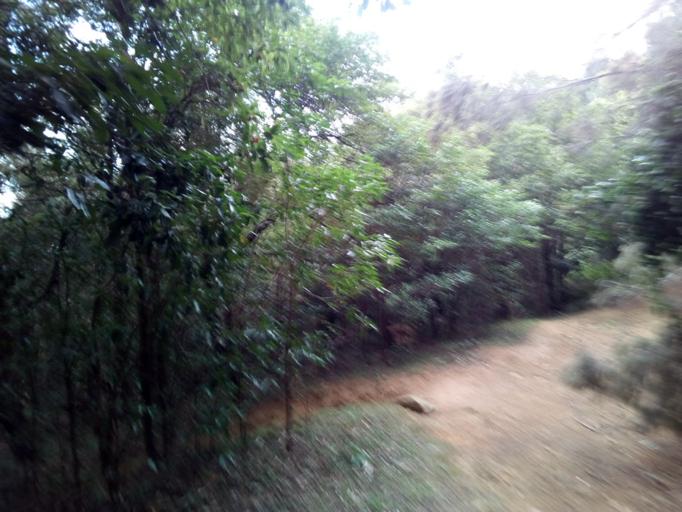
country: AU
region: New South Wales
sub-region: Wollongong
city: Keiraville
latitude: -34.4052
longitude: 150.8609
